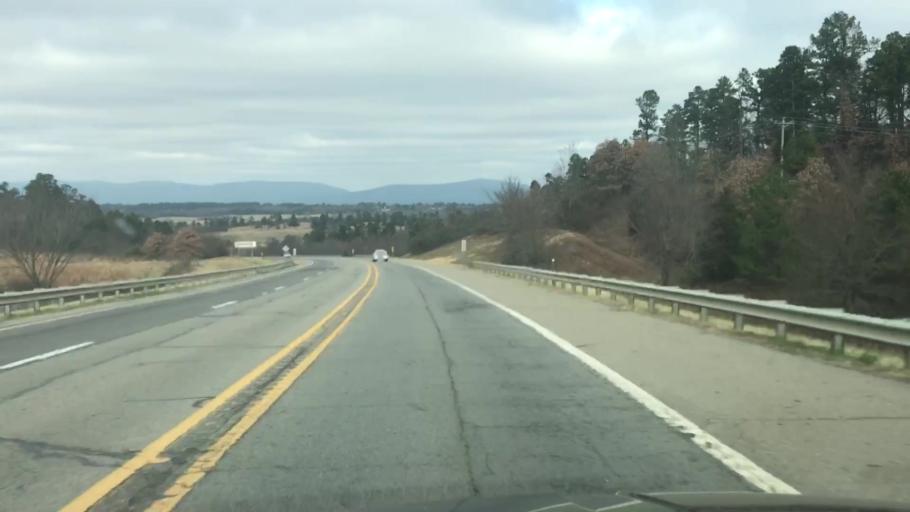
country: US
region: Arkansas
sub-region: Scott County
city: Waldron
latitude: 34.8648
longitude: -94.0742
